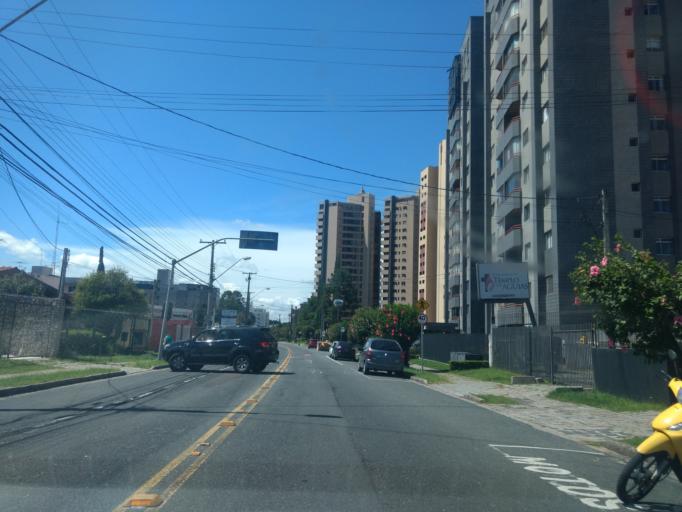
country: BR
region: Parana
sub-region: Curitiba
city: Curitiba
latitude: -25.4053
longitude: -49.2449
